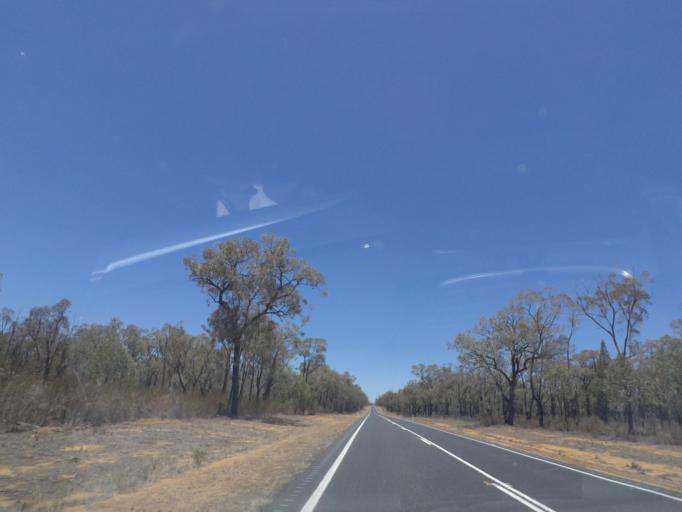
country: AU
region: New South Wales
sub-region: Narrabri
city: Narrabri
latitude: -30.7370
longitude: 149.5175
